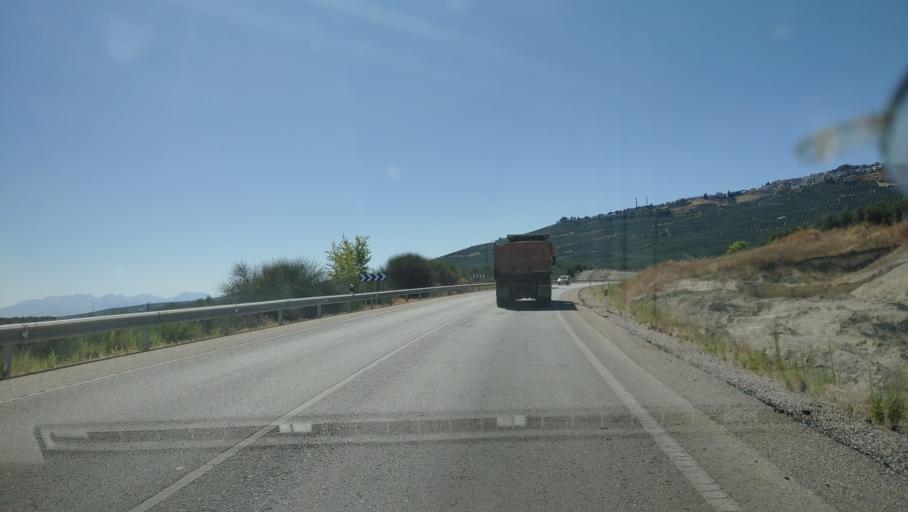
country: ES
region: Andalusia
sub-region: Provincia de Jaen
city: Villanueva del Arzobispo
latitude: 38.1551
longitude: -3.0058
